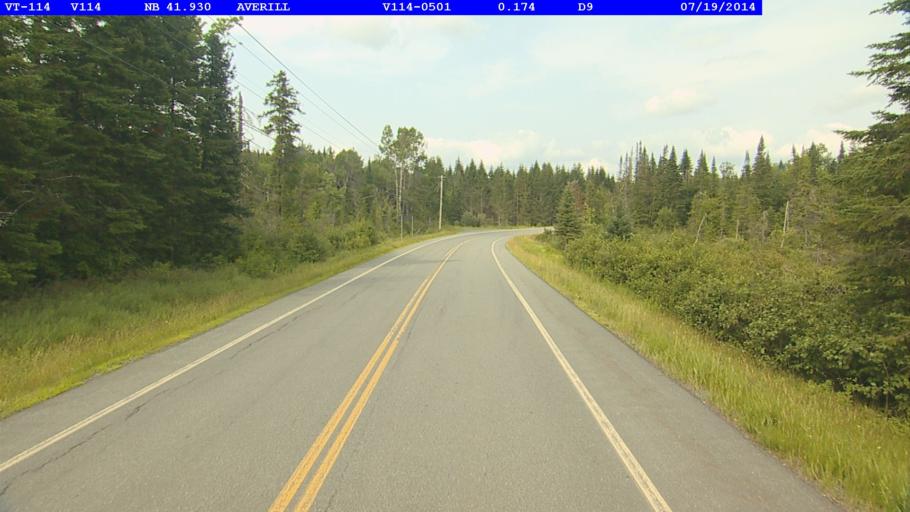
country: CA
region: Quebec
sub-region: Estrie
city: Coaticook
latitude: 45.0013
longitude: -71.7060
